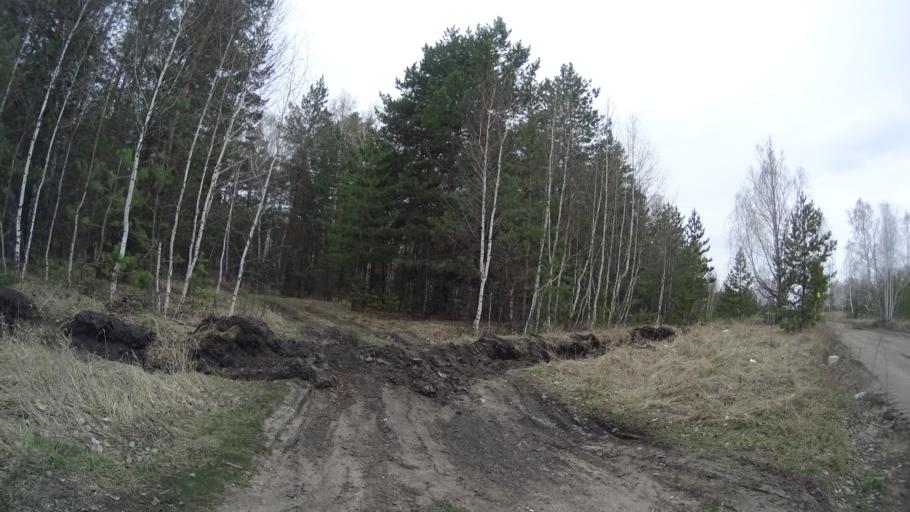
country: RU
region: Chelyabinsk
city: Yuzhnoural'sk
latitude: 54.4951
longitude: 61.2709
